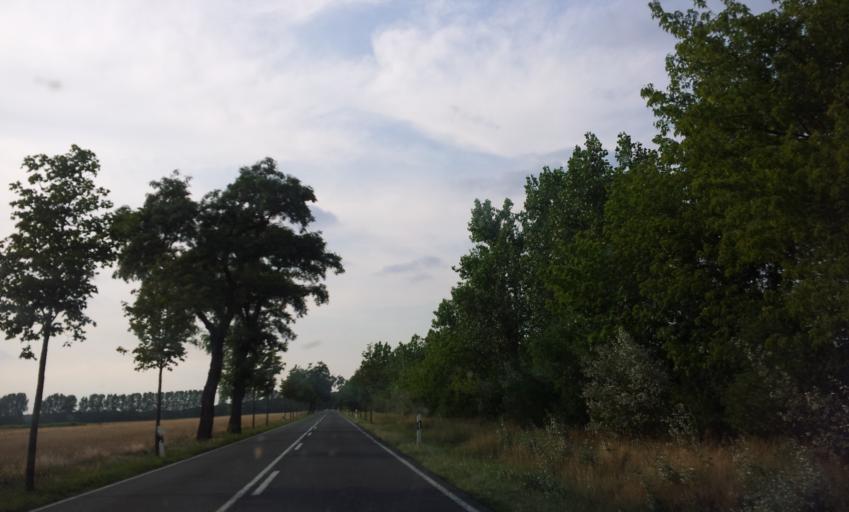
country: DE
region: Brandenburg
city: Beelitz
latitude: 52.1237
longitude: 13.0153
